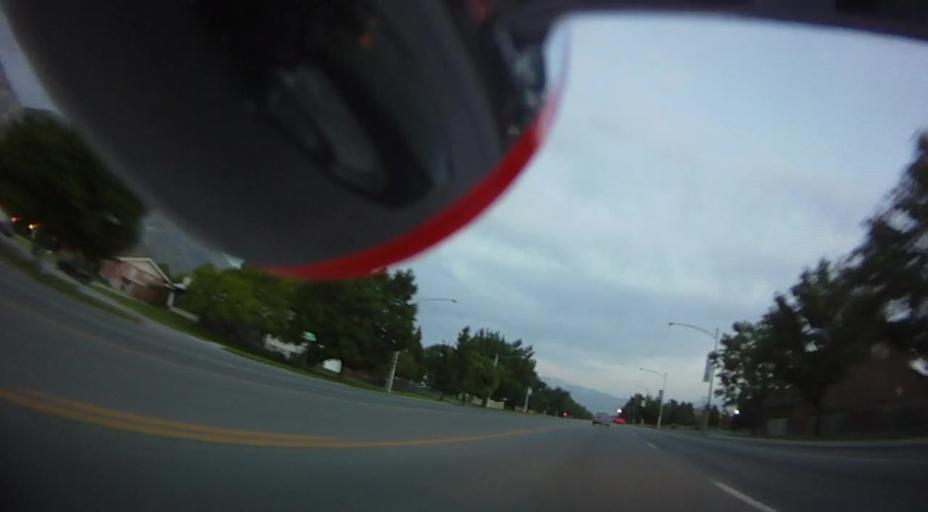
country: US
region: Utah
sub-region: Utah County
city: Provo
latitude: 40.2626
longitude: -111.6586
